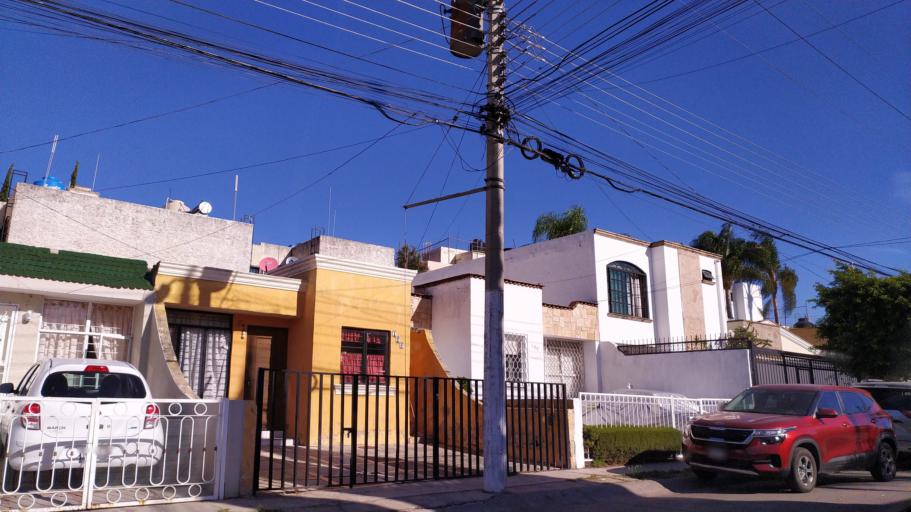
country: MX
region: Jalisco
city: Guadalajara
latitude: 20.6548
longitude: -103.4363
